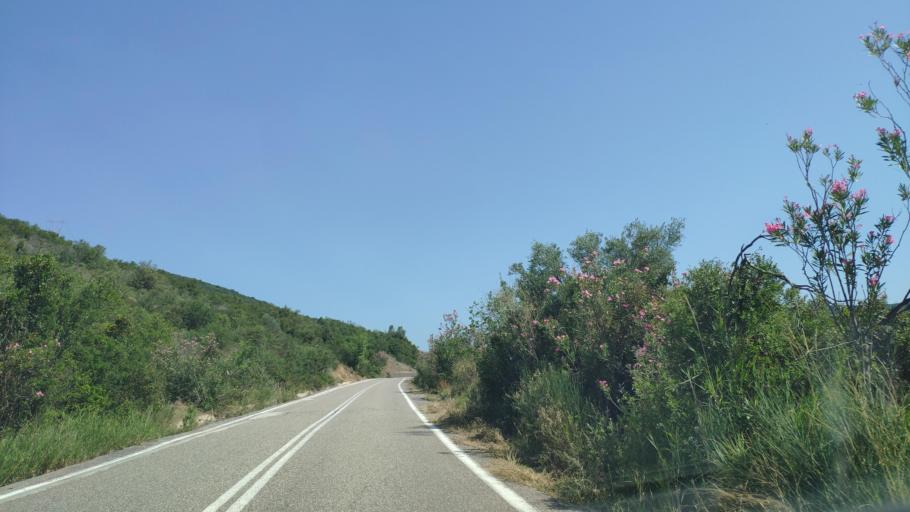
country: GR
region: West Greece
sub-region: Nomos Aitolias kai Akarnanias
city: Lepenou
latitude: 38.7582
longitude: 21.3393
